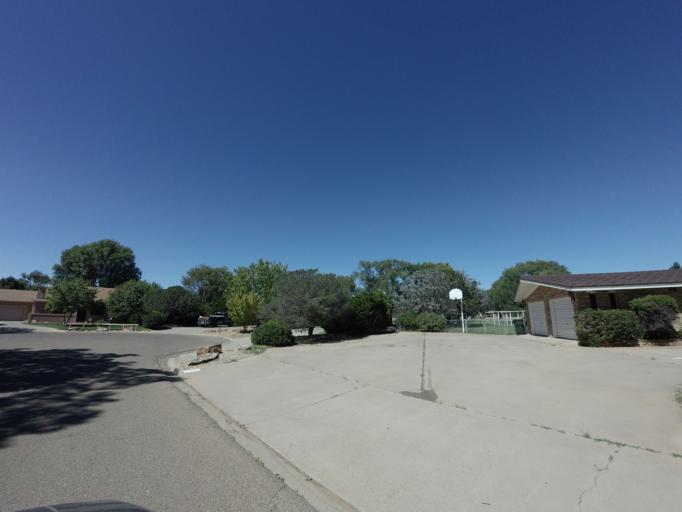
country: US
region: New Mexico
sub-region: Curry County
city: Clovis
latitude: 34.4383
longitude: -103.1857
